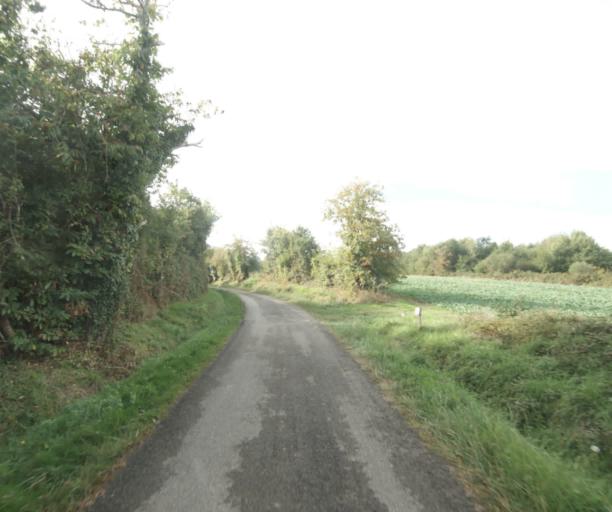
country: FR
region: Midi-Pyrenees
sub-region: Departement du Gers
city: Cazaubon
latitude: 43.8603
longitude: -0.1307
